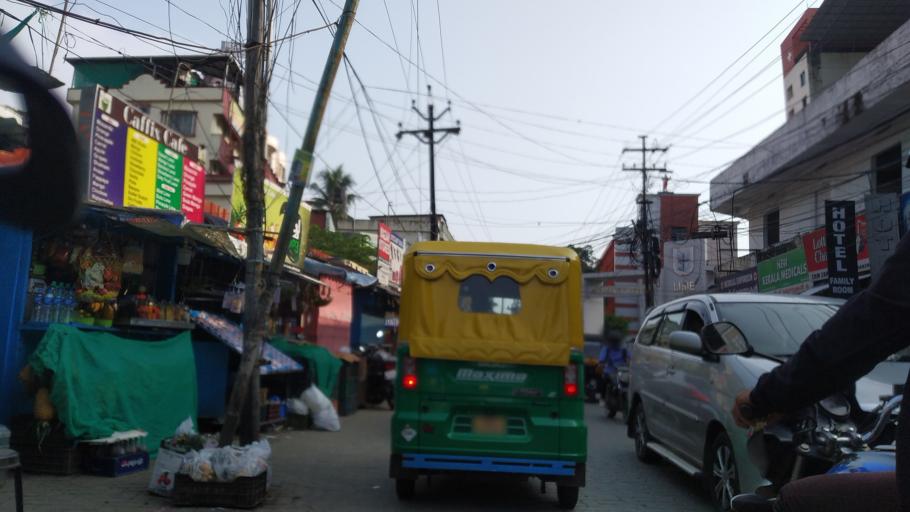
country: IN
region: Kerala
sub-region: Ernakulam
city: Cochin
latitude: 9.9892
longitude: 76.2885
